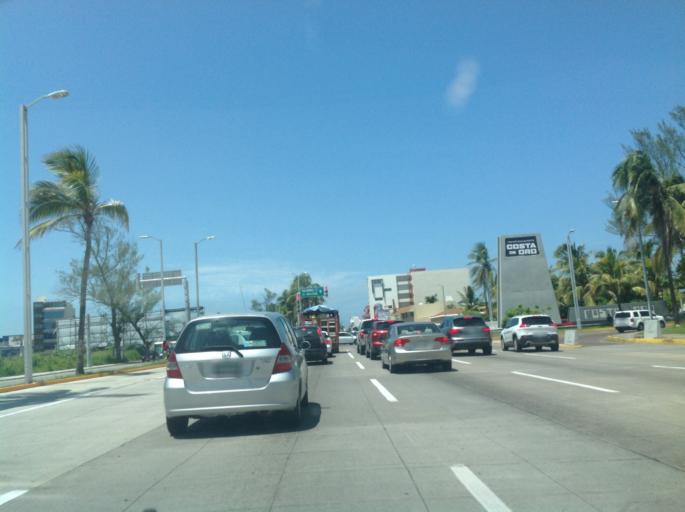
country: MX
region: Veracruz
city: Boca del Rio
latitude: 19.1454
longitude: -96.1039
